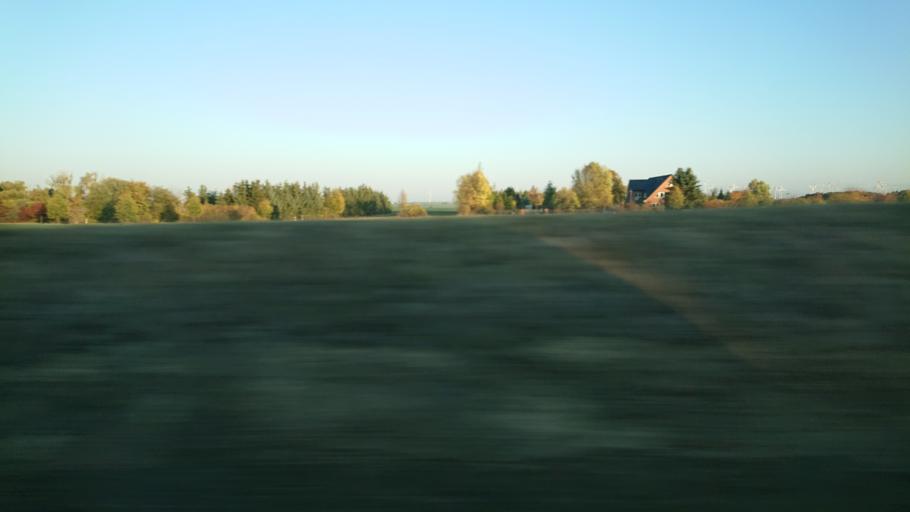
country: DE
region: Mecklenburg-Vorpommern
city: Neverin
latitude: 53.6573
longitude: 13.3182
